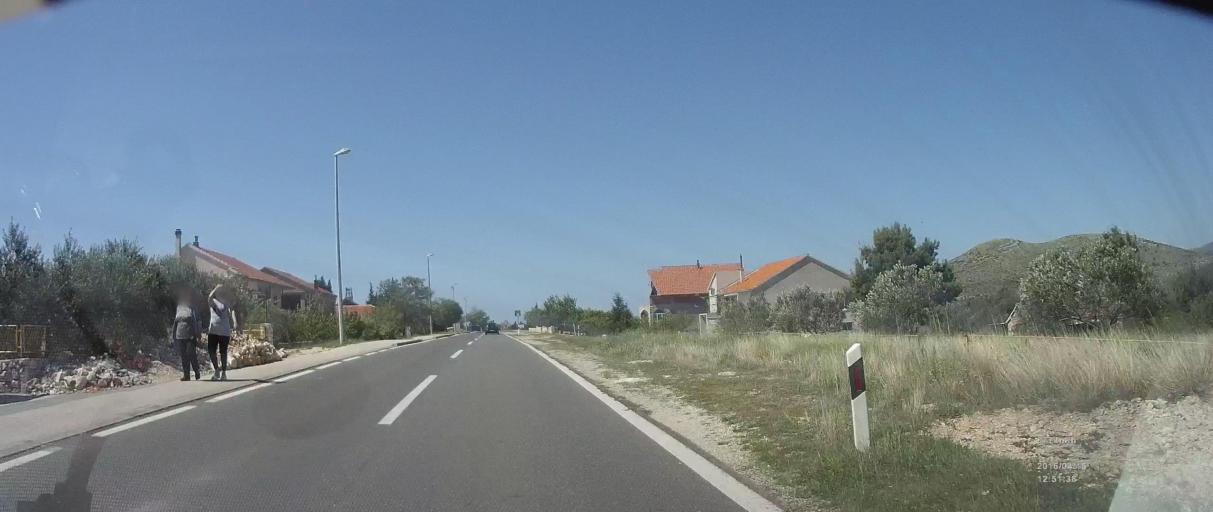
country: HR
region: Sibensko-Kniniska
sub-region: Grad Sibenik
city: Brodarica
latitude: 43.6756
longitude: 15.9990
